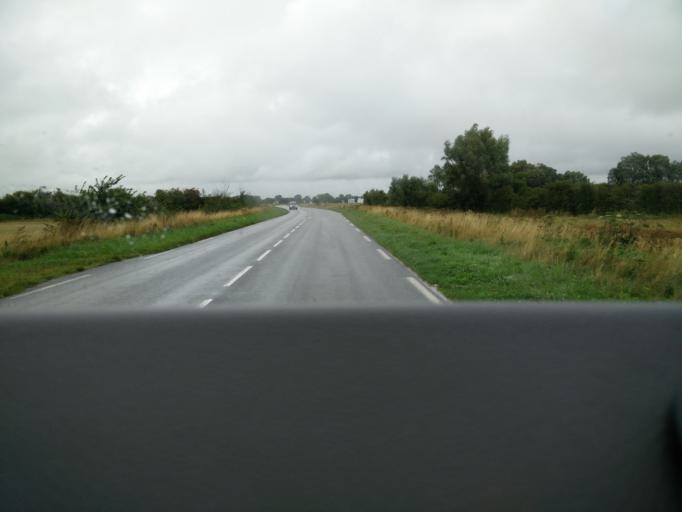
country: FR
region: Picardie
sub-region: Departement de la Somme
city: Le Crotoy
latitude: 50.2328
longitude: 1.6438
